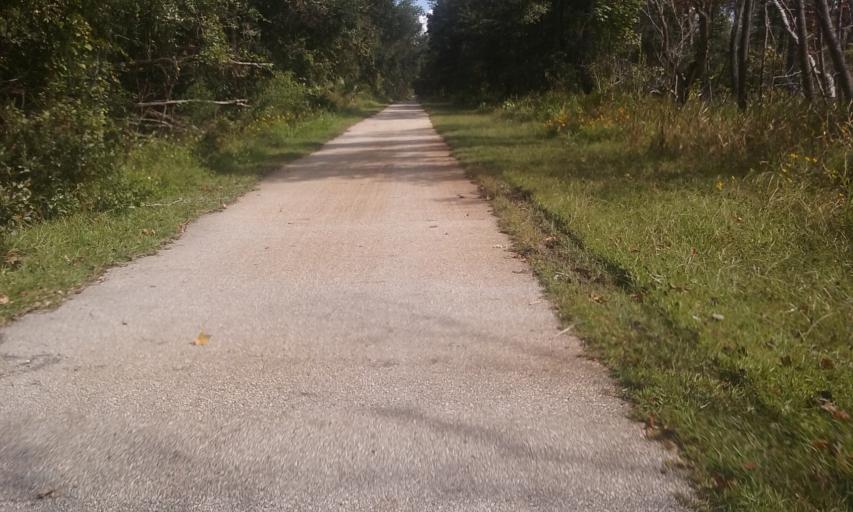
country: US
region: Florida
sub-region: Alachua County
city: Hawthorne
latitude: 29.5915
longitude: -82.1781
